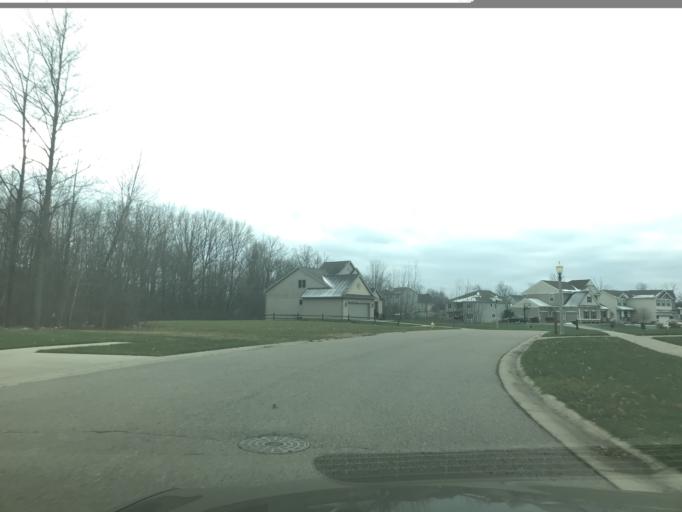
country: US
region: Michigan
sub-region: Eaton County
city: Waverly
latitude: 42.7195
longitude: -84.6781
